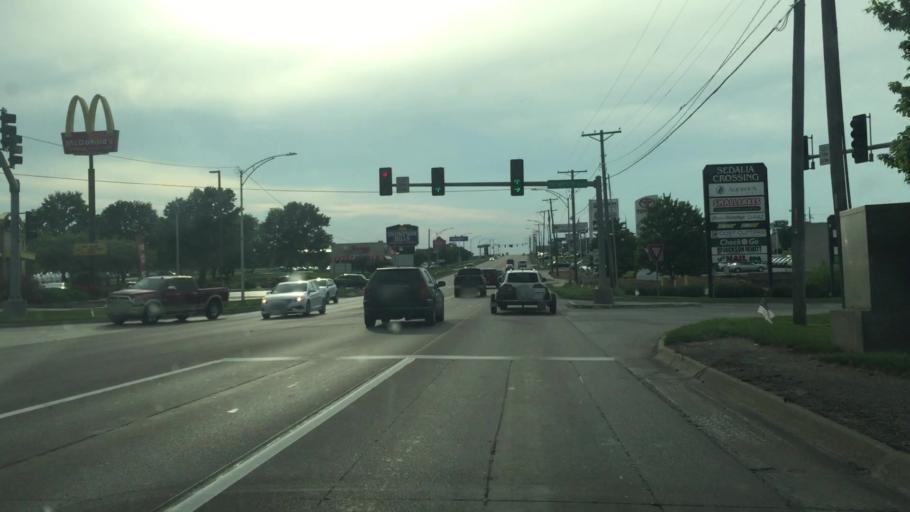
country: US
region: Missouri
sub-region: Pettis County
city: Sedalia
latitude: 38.7084
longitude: -93.2647
